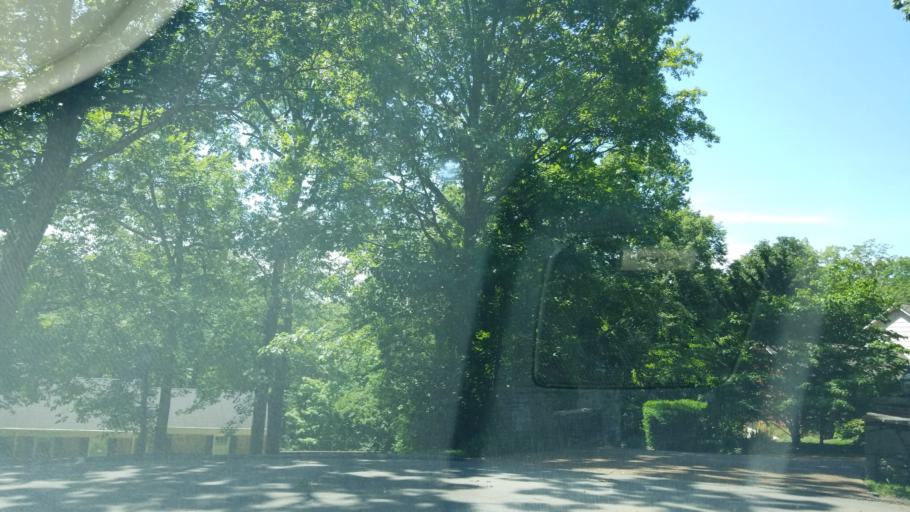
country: US
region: Tennessee
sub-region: Davidson County
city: Forest Hills
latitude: 36.0605
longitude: -86.8116
